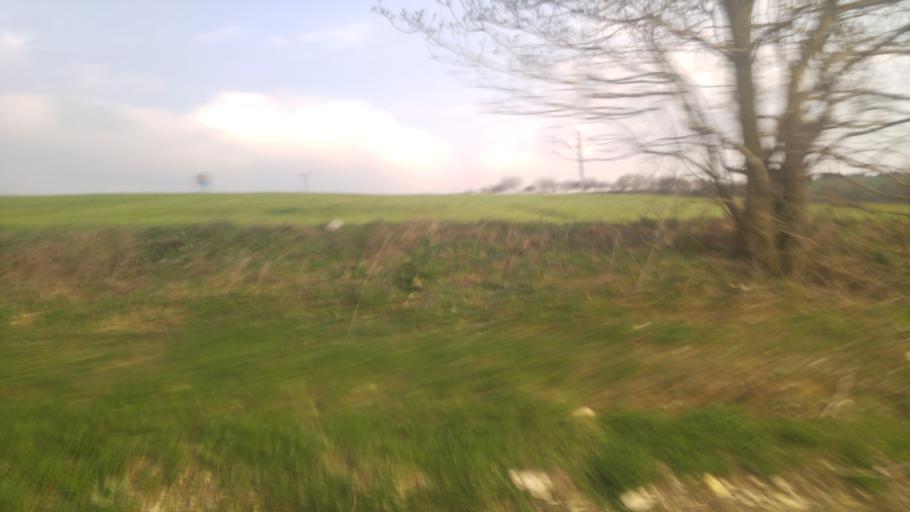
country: TR
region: Istanbul
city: Ortakoy
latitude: 41.1337
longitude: 28.3572
